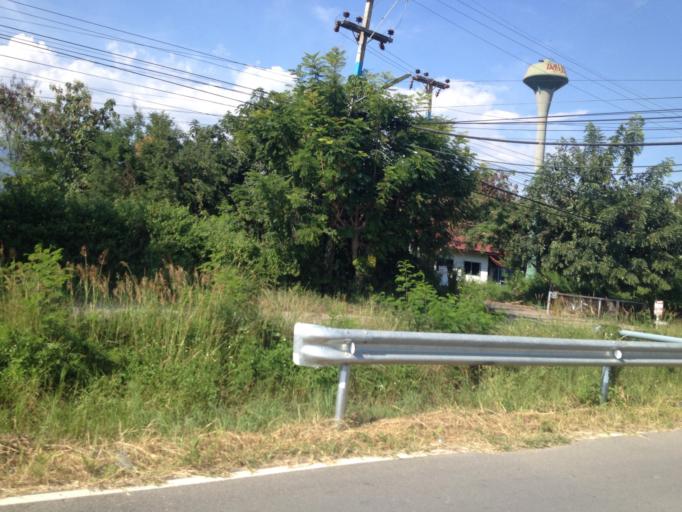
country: TH
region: Chiang Mai
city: Hang Dong
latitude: 18.7284
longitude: 98.9550
